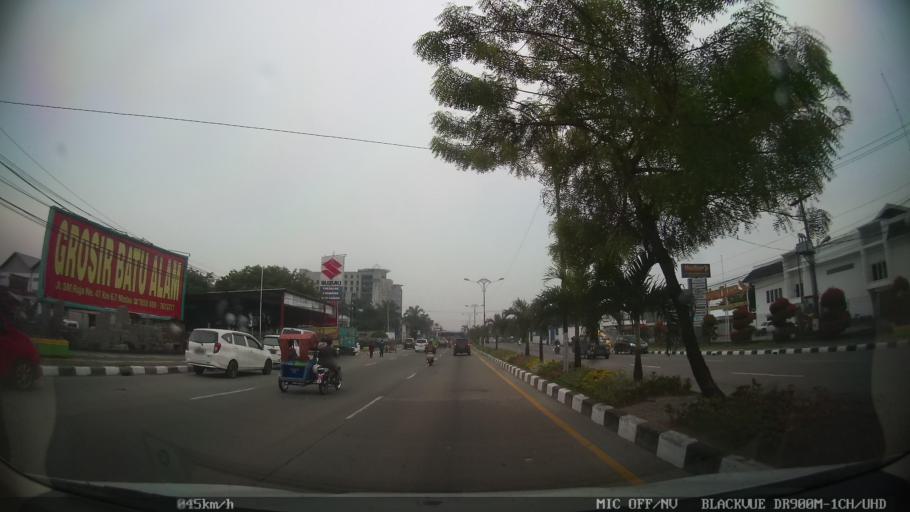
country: ID
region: North Sumatra
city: Deli Tua
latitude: 3.5387
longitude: 98.7038
